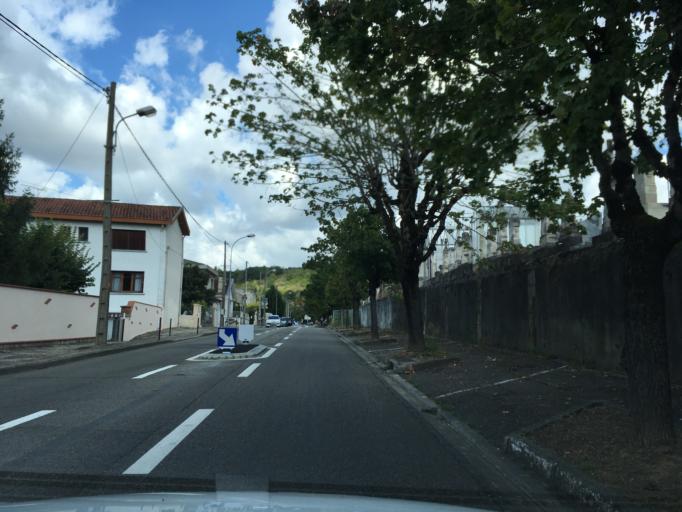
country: FR
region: Aquitaine
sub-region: Departement du Lot-et-Garonne
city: Agen
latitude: 44.2129
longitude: 0.6284
